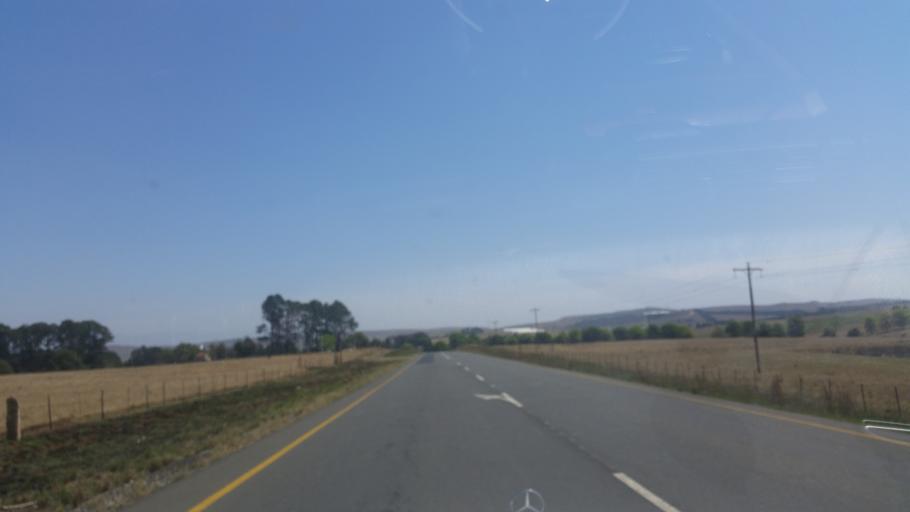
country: ZA
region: KwaZulu-Natal
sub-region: uMgungundlovu District Municipality
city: Mooirivier
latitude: -29.1493
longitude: 29.9819
